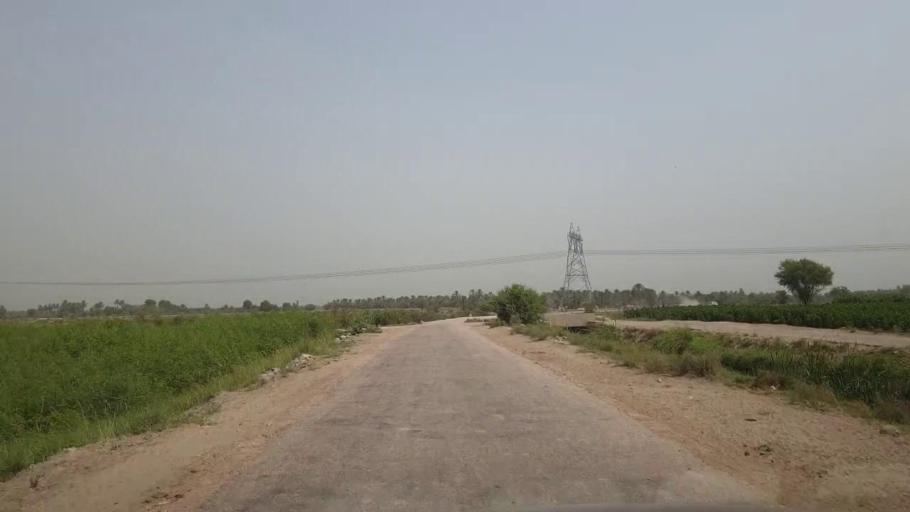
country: PK
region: Sindh
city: Gambat
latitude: 27.4113
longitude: 68.5500
